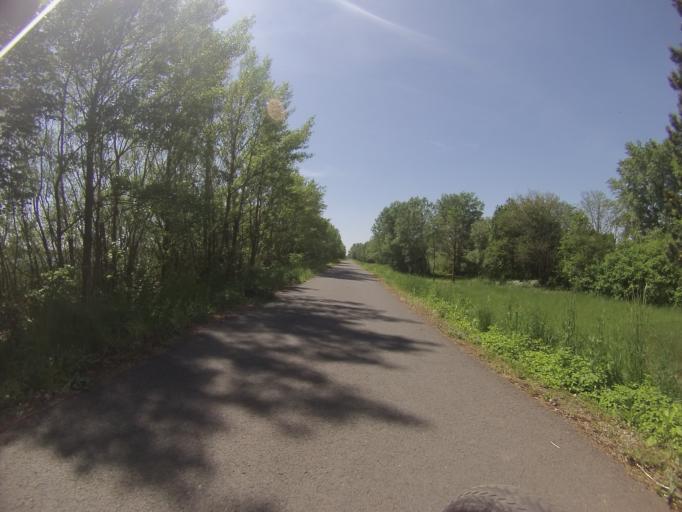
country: CZ
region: South Moravian
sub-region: Okres Breclav
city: Dolni Dunajovice
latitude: 48.9053
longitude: 16.5911
